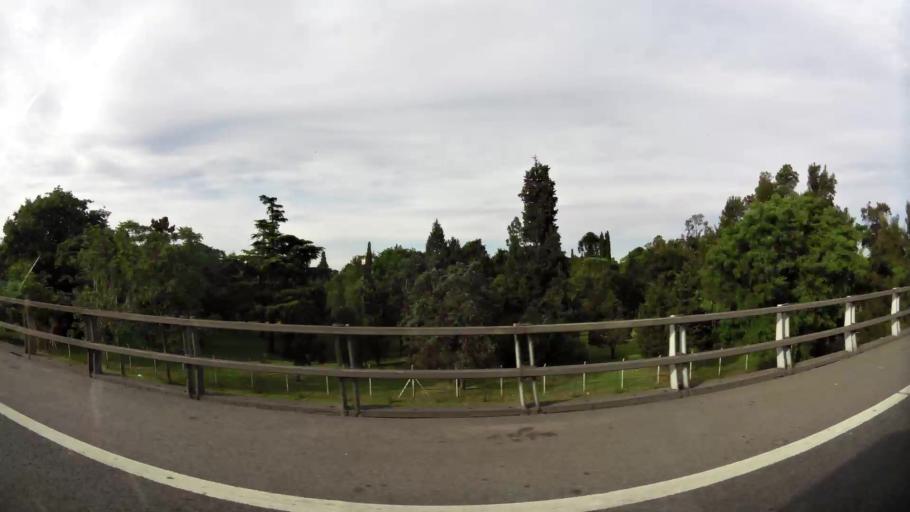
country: AR
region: Buenos Aires F.D.
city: Villa Lugano
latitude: -34.6466
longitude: -58.4828
